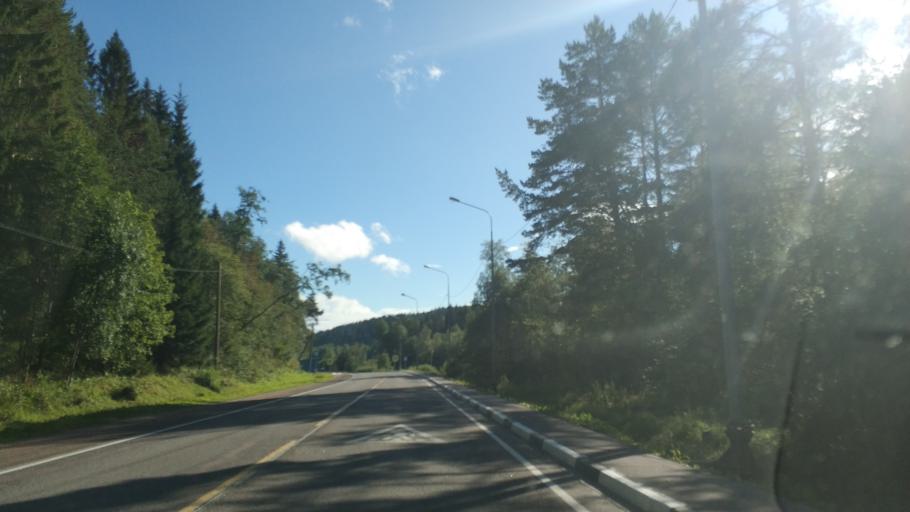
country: RU
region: Republic of Karelia
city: Sortavala
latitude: 61.6734
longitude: 30.6544
